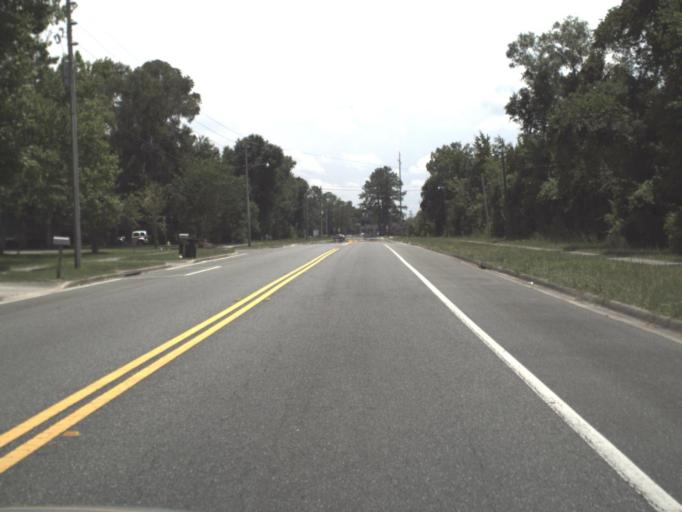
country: US
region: Florida
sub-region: Bradford County
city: Starke
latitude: 29.9553
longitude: -82.1140
